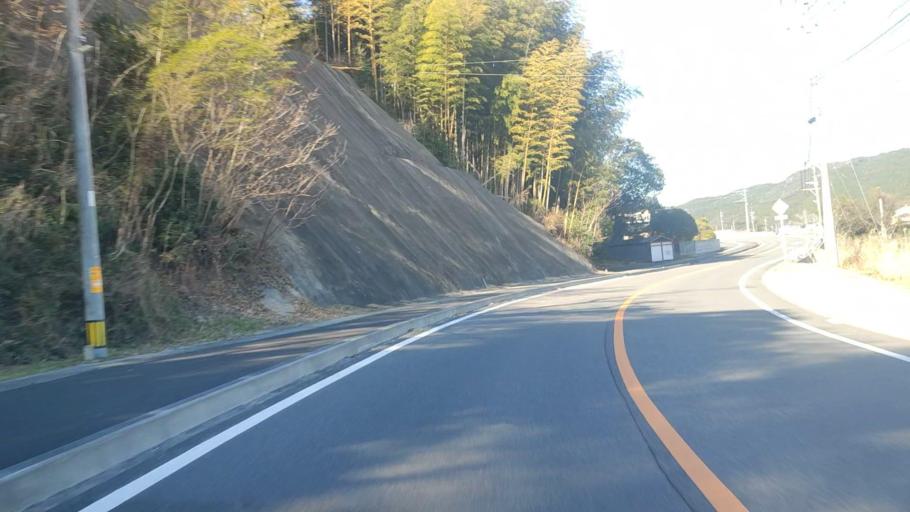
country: JP
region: Oita
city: Saiki
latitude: 32.9261
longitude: 131.9232
